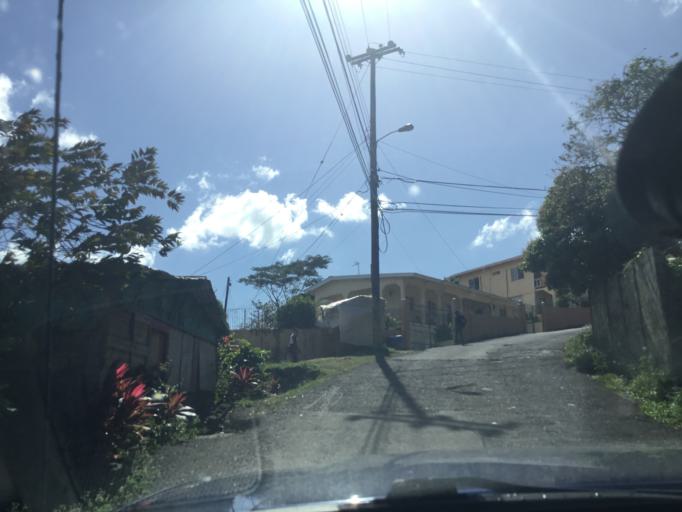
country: VC
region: Saint George
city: Kingstown Park
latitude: 13.1729
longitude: -61.2501
